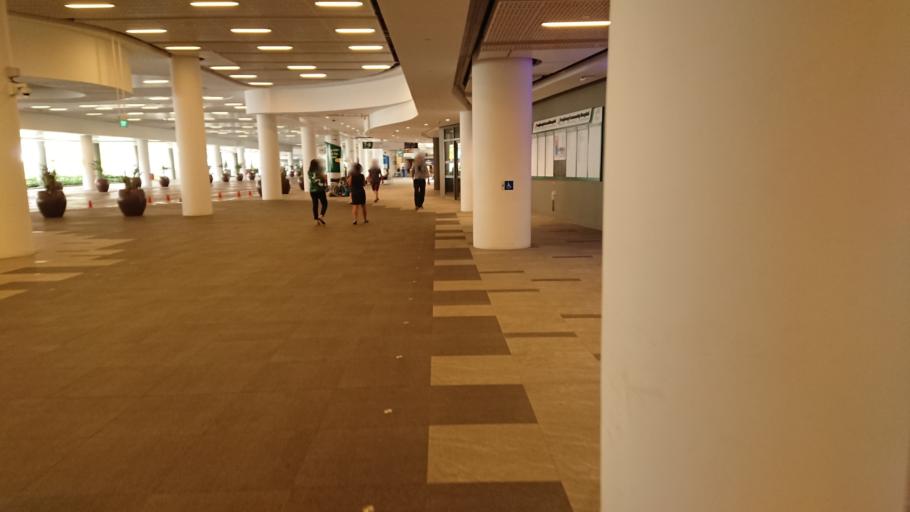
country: MY
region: Johor
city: Kampung Pasir Gudang Baru
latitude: 1.3959
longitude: 103.8919
